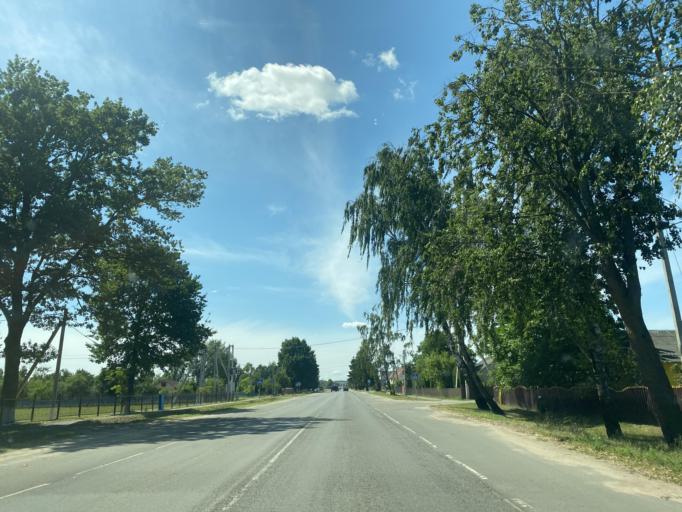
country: BY
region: Brest
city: Ivanava
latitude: 52.1619
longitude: 25.5467
